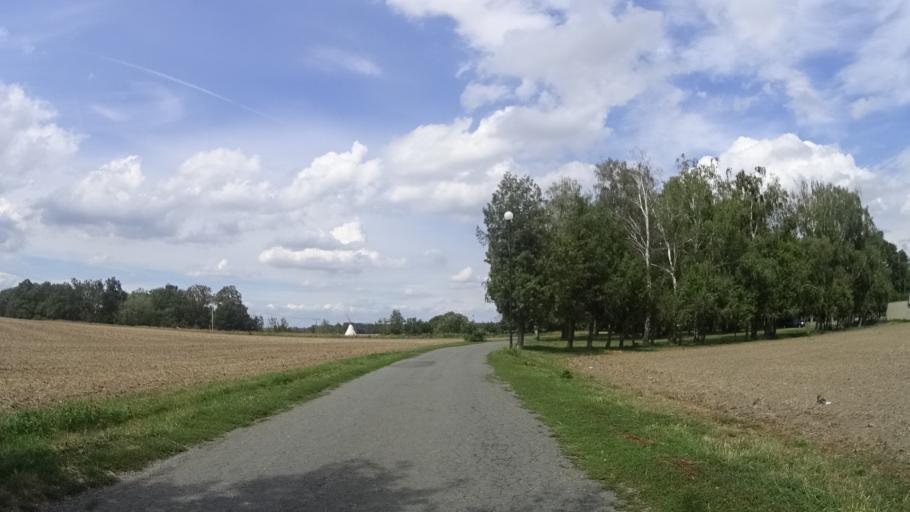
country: CZ
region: Olomoucky
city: Horka nad Moravou
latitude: 49.6421
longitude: 17.1973
